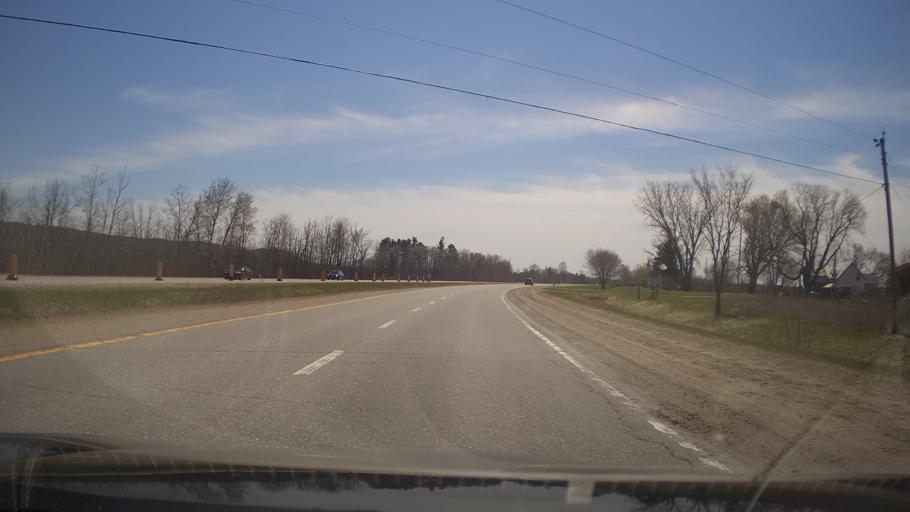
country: CA
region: Quebec
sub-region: Outaouais
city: Wakefield
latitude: 45.5243
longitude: -75.9943
